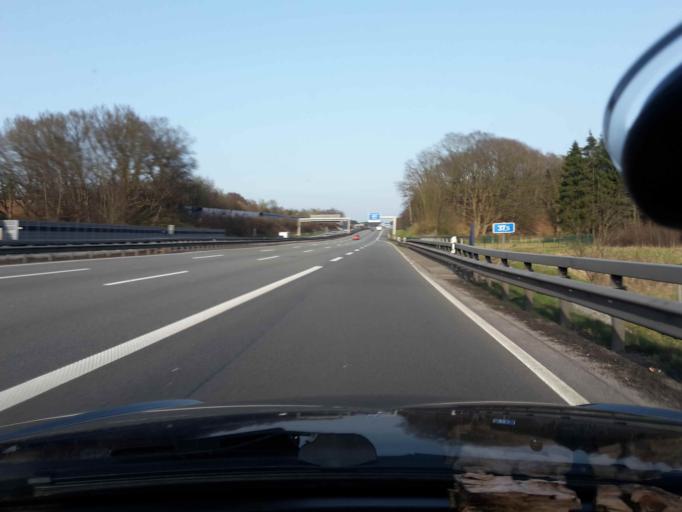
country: DE
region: Lower Saxony
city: Hollenstedt
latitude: 53.3595
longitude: 9.7145
